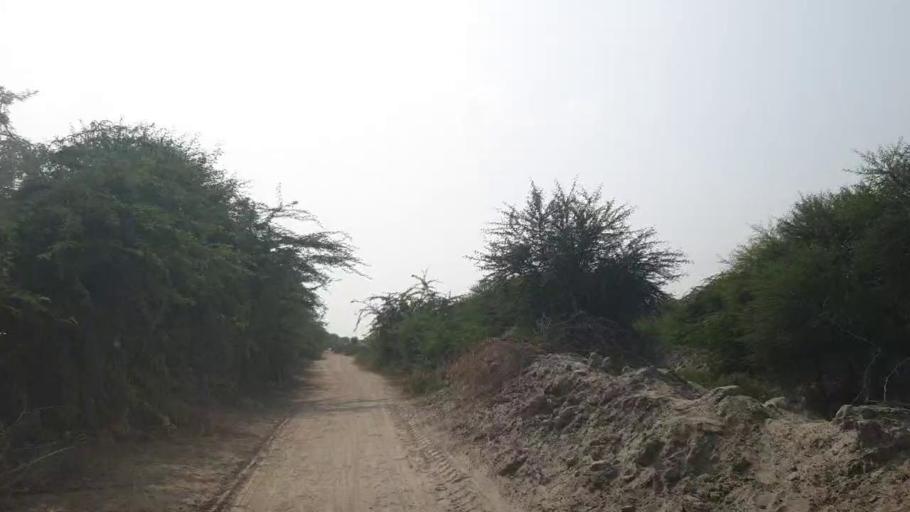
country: PK
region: Sindh
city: Badin
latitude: 24.6046
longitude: 68.7197
